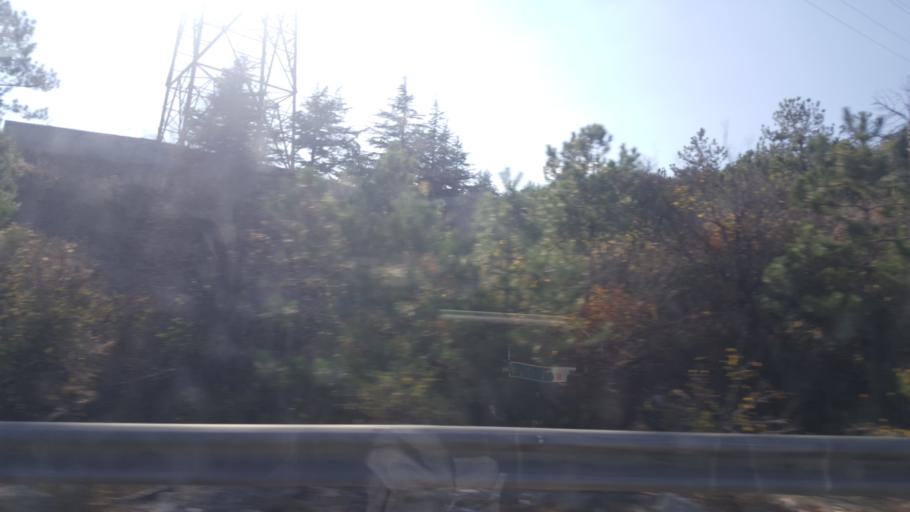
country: TR
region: Ankara
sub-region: Goelbasi
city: Golbasi
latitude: 39.8124
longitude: 32.8008
